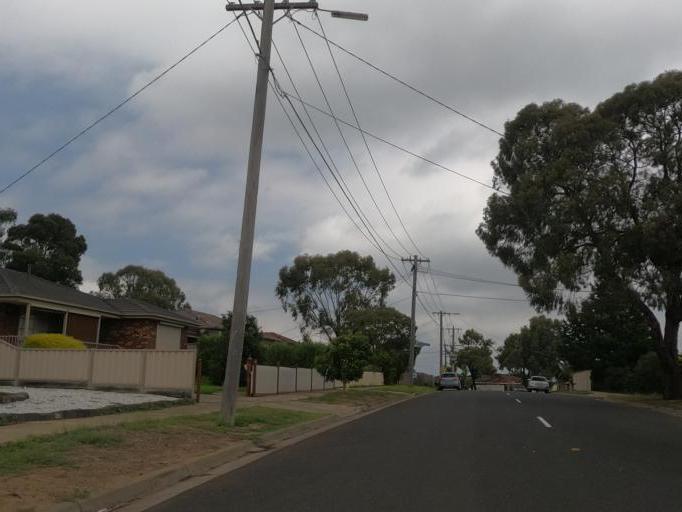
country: AU
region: Victoria
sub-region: Hume
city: Attwood
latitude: -37.6723
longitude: 144.8986
